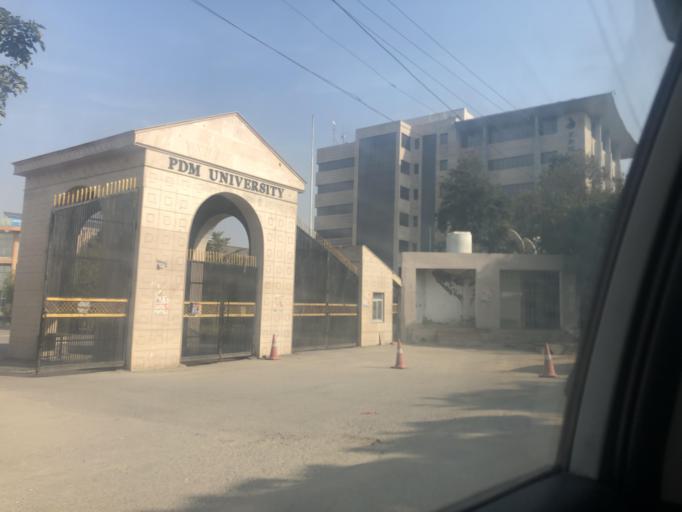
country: IN
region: Haryana
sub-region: Jhajjar
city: Bahadurgarh
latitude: 28.6871
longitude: 76.8889
